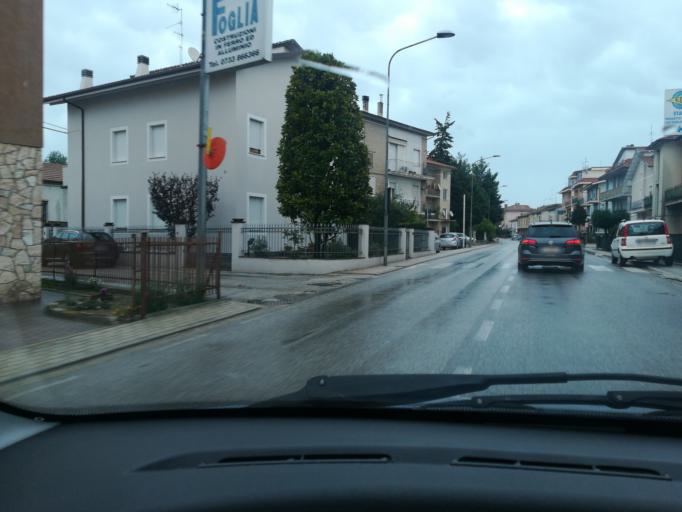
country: IT
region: The Marches
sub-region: Provincia di Macerata
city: Borgo Stazione
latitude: 43.2833
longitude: 13.6402
